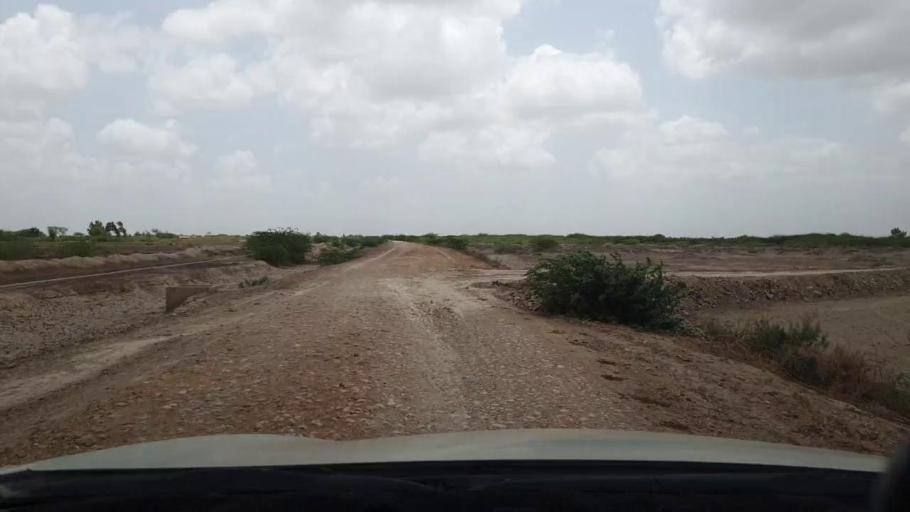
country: PK
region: Sindh
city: Kadhan
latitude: 24.3869
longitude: 68.9331
